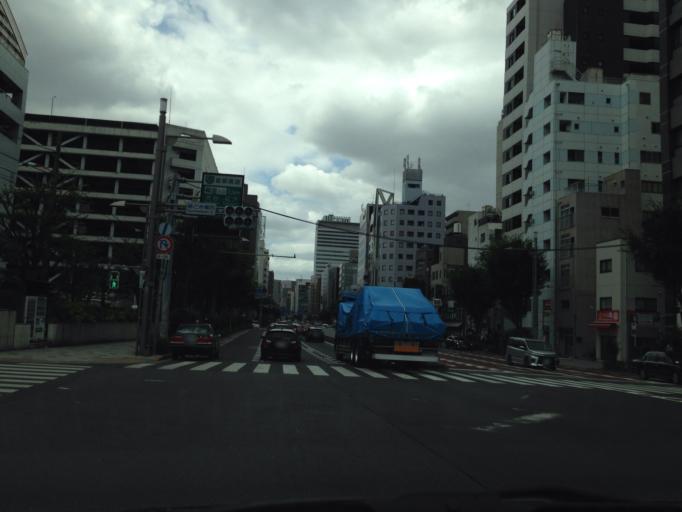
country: JP
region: Tokyo
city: Tokyo
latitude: 35.6634
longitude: 139.7738
